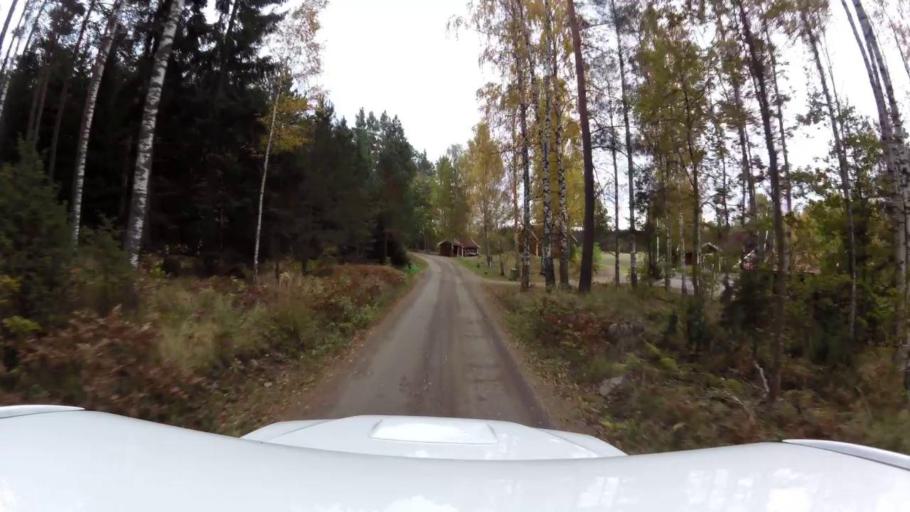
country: SE
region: OEstergoetland
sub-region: Linkopings Kommun
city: Ljungsbro
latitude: 58.5431
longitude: 15.4414
